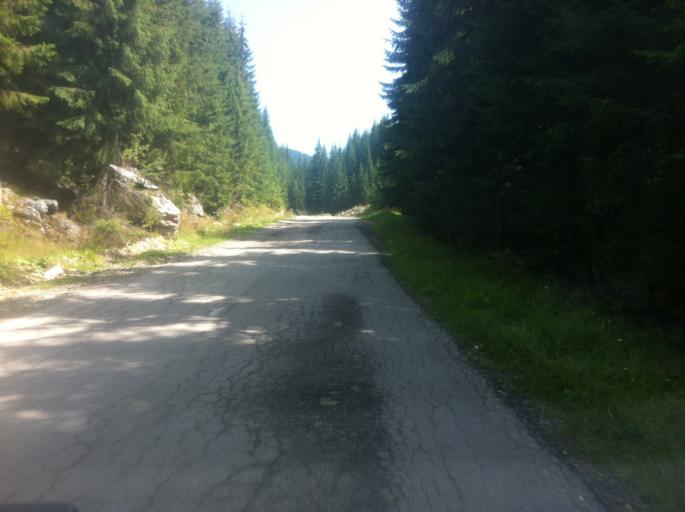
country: RO
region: Hunedoara
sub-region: Oras Petrila
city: Petrila
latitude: 45.4061
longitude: 23.5664
